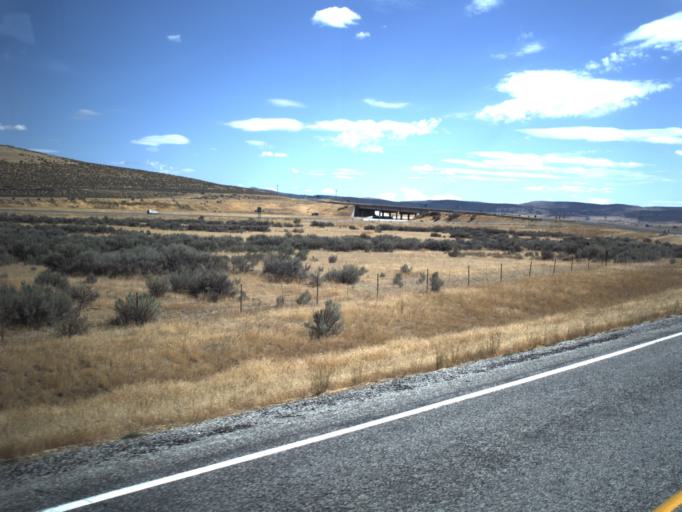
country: US
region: Idaho
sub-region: Oneida County
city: Malad City
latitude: 41.9640
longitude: -112.7643
